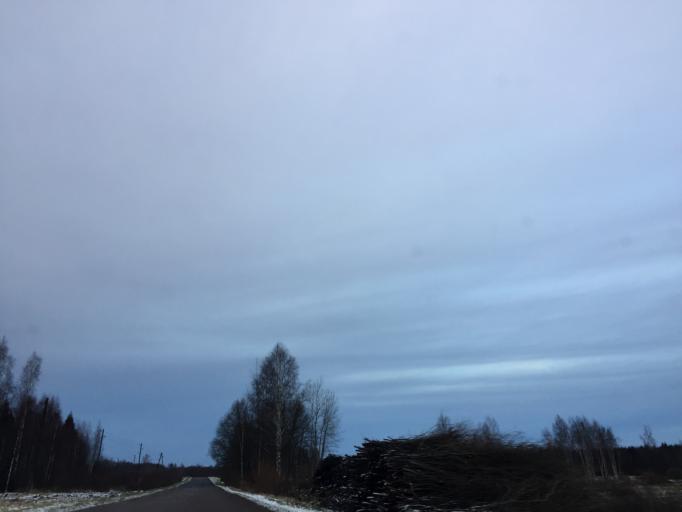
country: LV
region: Aloja
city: Aloja
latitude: 57.6346
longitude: 24.9382
